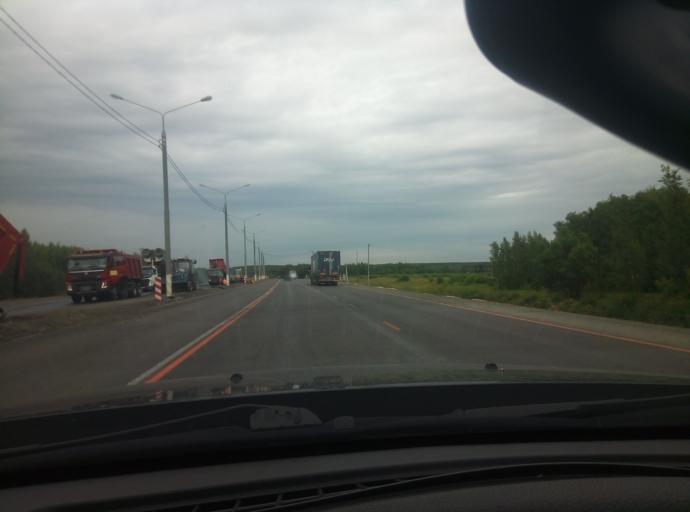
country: RU
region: Tula
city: Yasnogorsk
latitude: 54.5310
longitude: 37.5175
